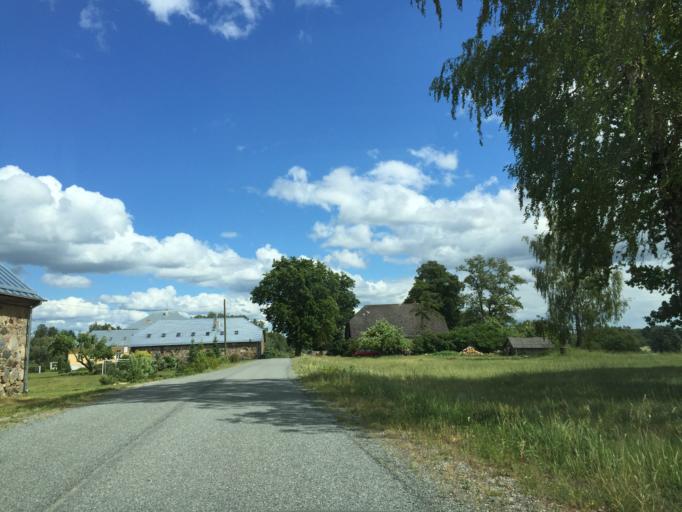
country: LV
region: Vecumnieki
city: Vecumnieki
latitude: 56.4686
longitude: 24.4402
